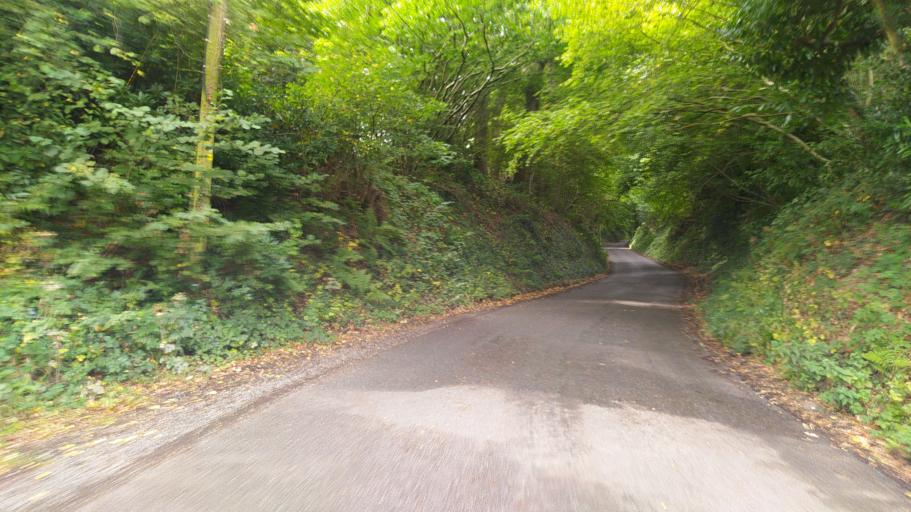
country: GB
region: England
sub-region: Hampshire
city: Petersfield
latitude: 50.9888
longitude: -0.9243
